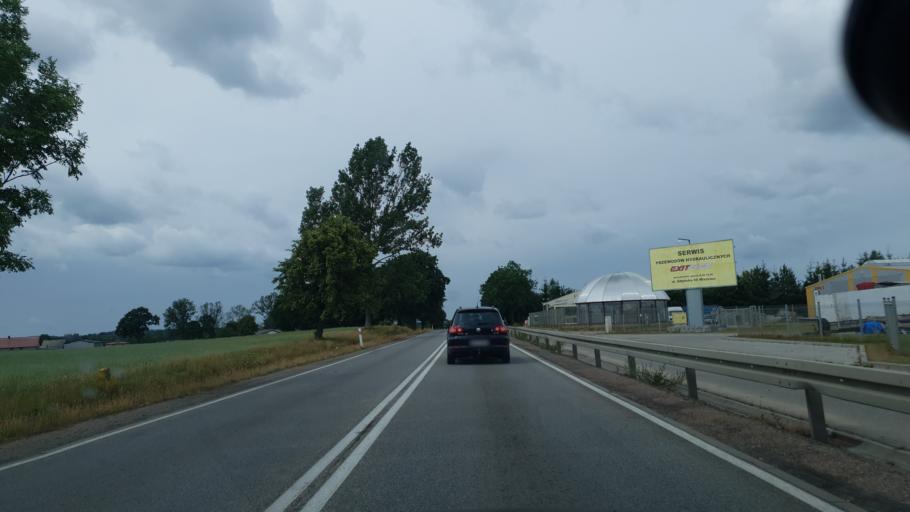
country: PL
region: Pomeranian Voivodeship
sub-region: Powiat kartuski
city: Zukowo
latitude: 54.3841
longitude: 18.3611
